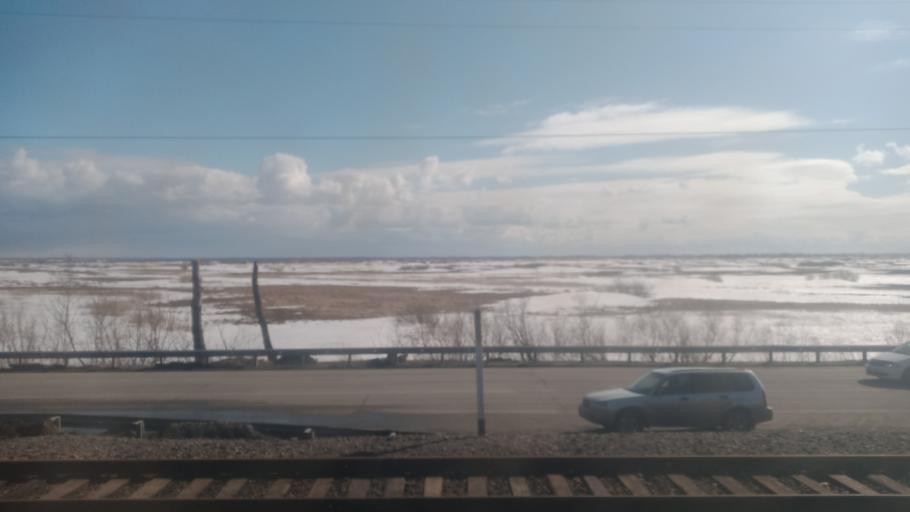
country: RU
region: Altai Krai
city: Novoaltaysk
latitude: 53.3718
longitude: 83.8767
